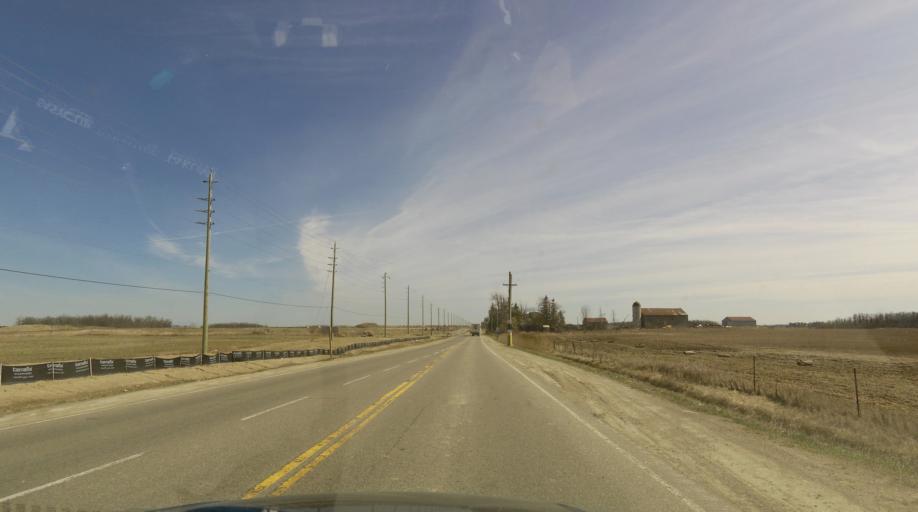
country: CA
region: Ontario
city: Brampton
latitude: 43.6943
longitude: -79.8669
